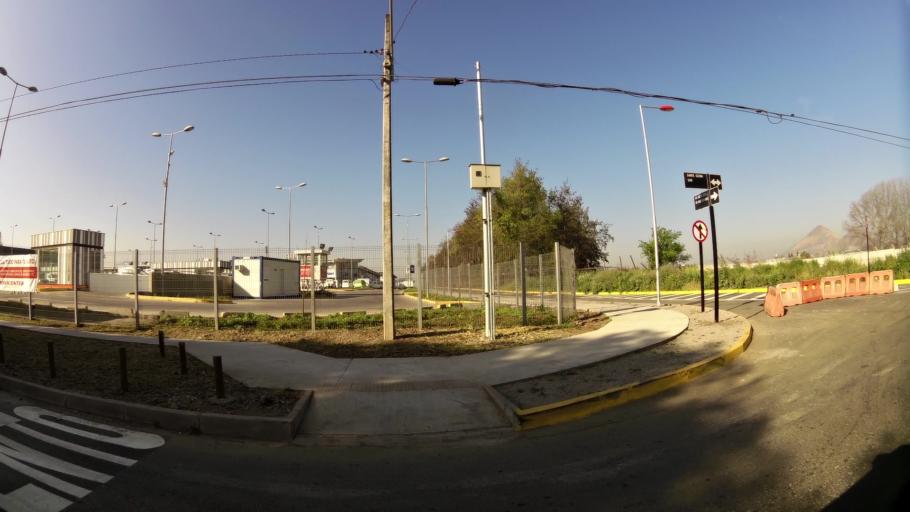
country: CL
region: Santiago Metropolitan
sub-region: Provincia de Chacabuco
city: Chicureo Abajo
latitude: -33.3685
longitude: -70.6650
